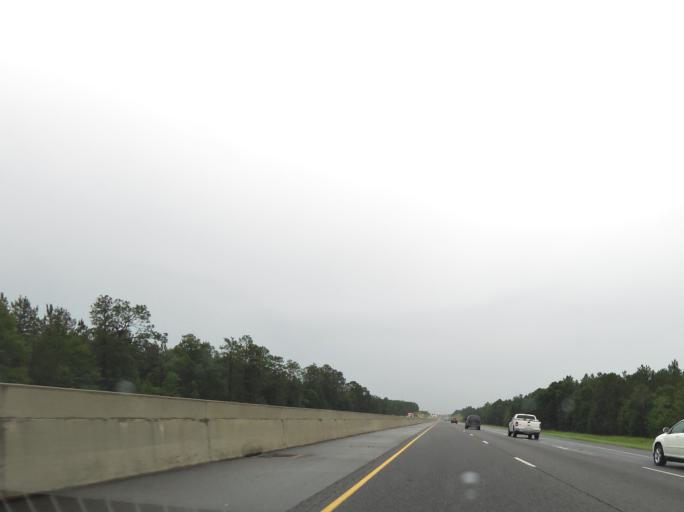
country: US
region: Georgia
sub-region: Turner County
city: Ashburn
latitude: 31.7676
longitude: -83.6761
